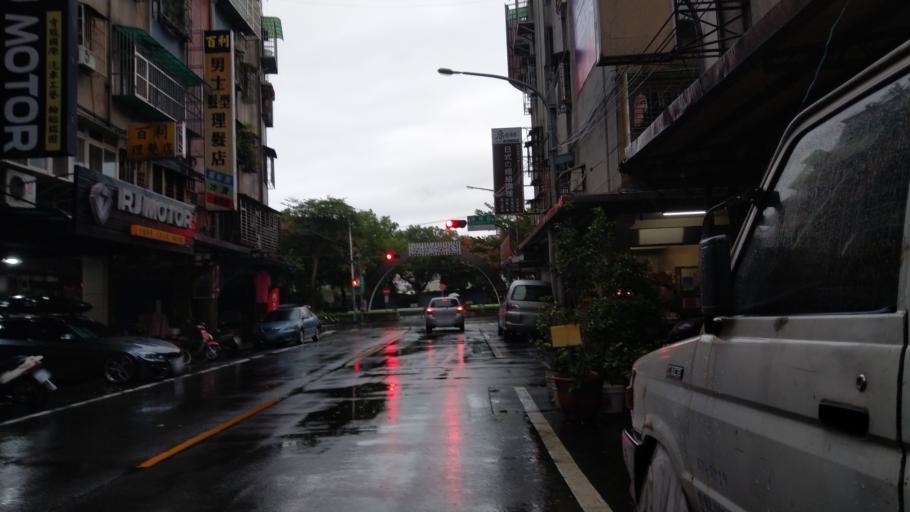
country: TW
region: Taipei
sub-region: Taipei
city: Banqiao
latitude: 24.9933
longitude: 121.4649
